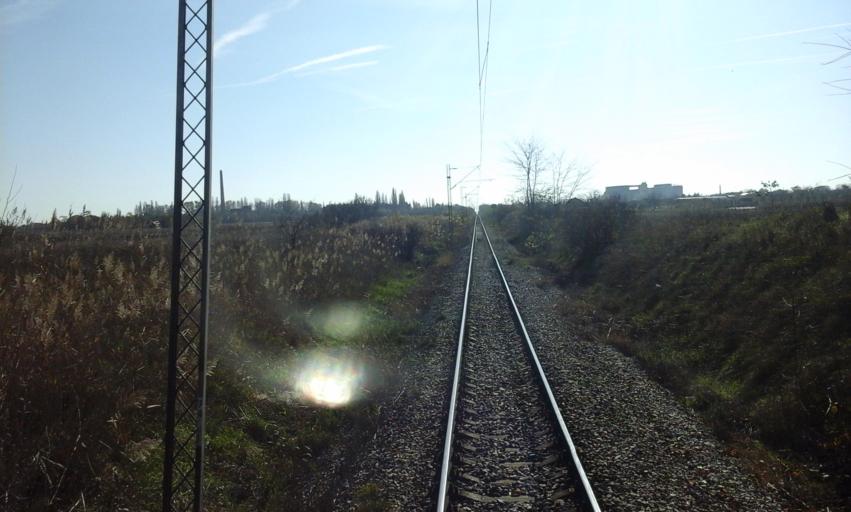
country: RS
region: Autonomna Pokrajina Vojvodina
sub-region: Severnobacki Okrug
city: Subotica
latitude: 46.0765
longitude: 19.6894
